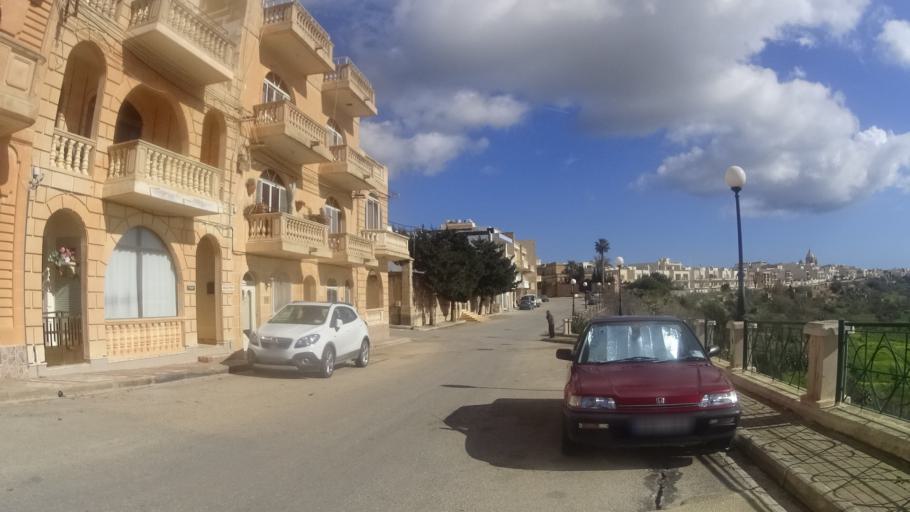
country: MT
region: In-Nadur
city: Nadur
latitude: 36.0361
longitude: 14.2855
